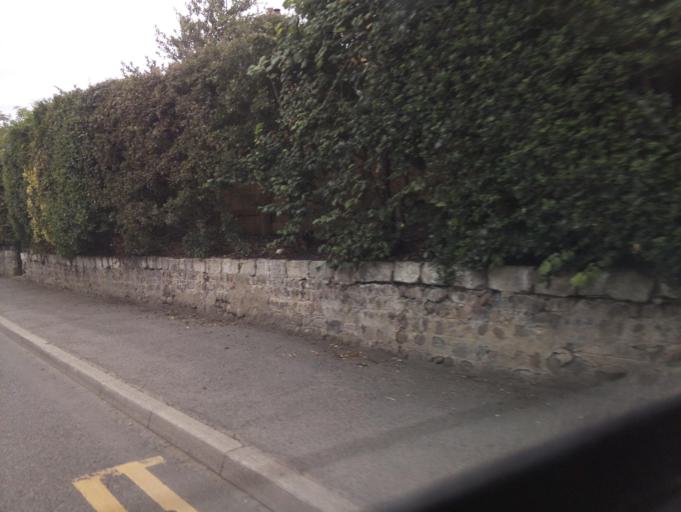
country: GB
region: England
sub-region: North Yorkshire
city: Ripon
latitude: 54.1424
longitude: -1.5238
